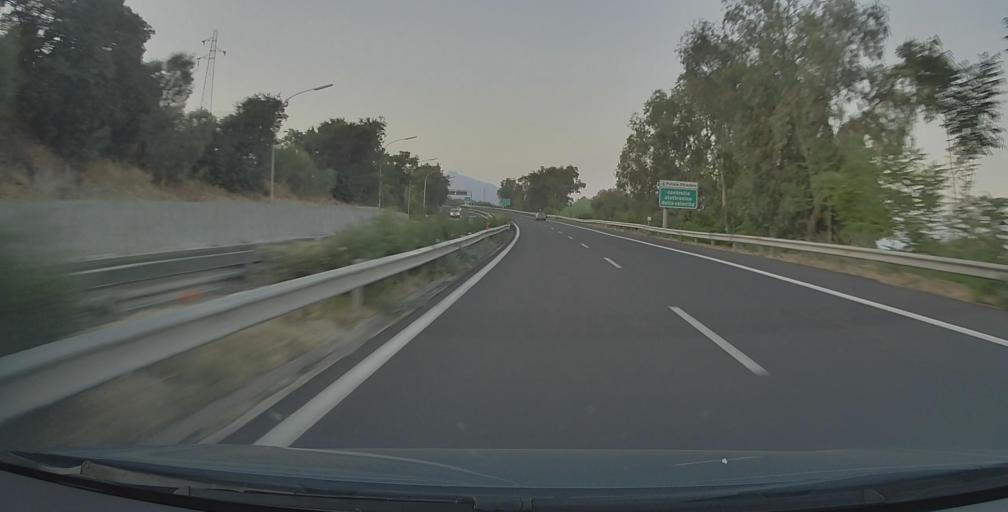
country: IT
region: Sicily
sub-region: Catania
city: Fiumefreddo Sicilia
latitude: 37.7985
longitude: 15.1959
